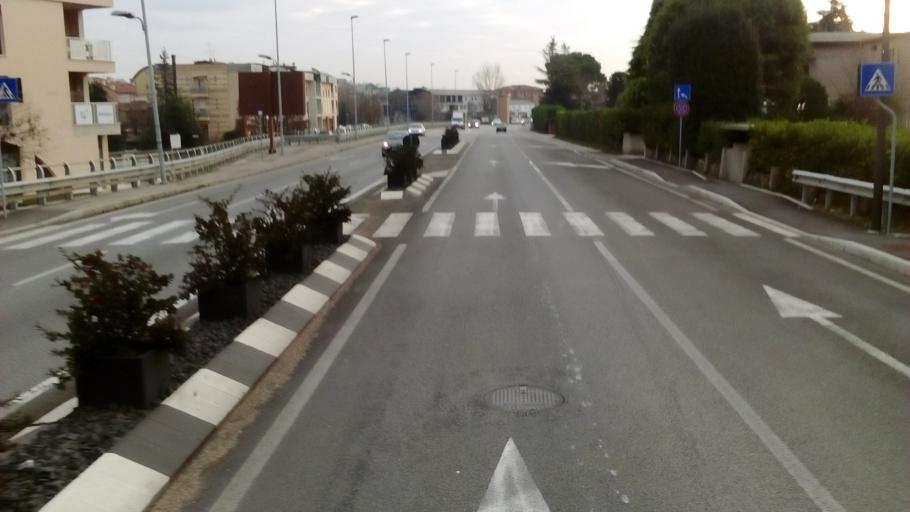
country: IT
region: Veneto
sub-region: Provincia di Vicenza
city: Arzignano
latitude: 45.5169
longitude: 11.3345
